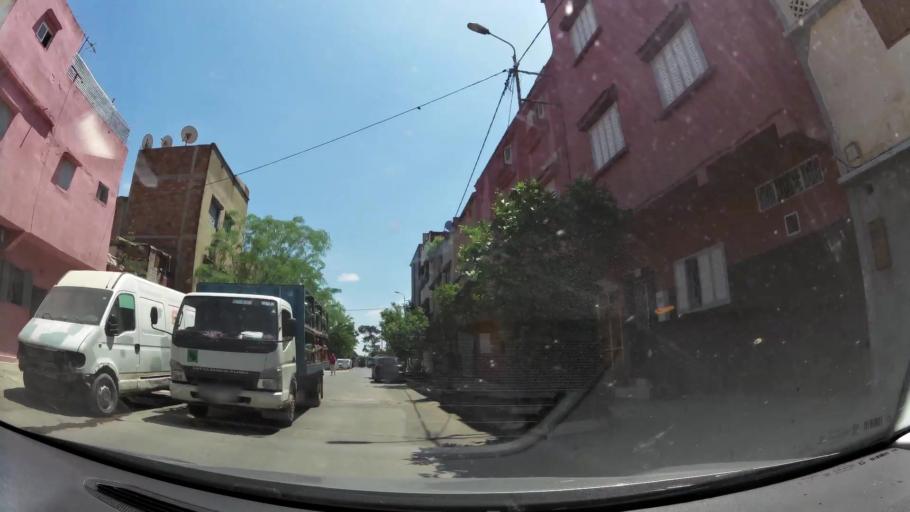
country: MA
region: Gharb-Chrarda-Beni Hssen
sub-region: Kenitra Province
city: Kenitra
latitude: 34.2555
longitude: -6.5597
